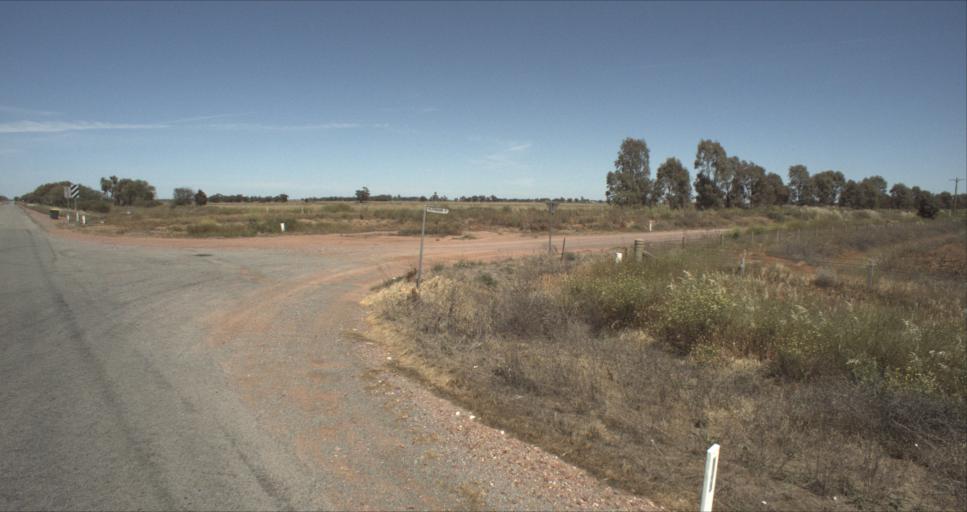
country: AU
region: New South Wales
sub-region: Leeton
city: Leeton
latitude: -34.4402
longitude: 146.2979
